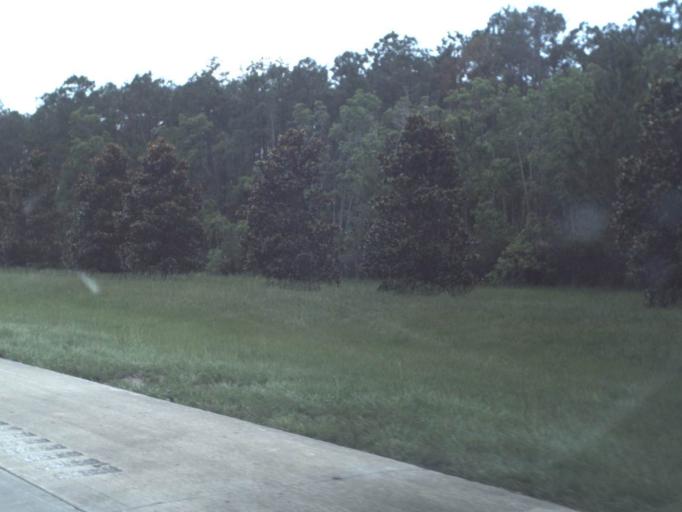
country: US
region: Florida
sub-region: Saint Johns County
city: Palm Valley
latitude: 30.1958
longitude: -81.5139
